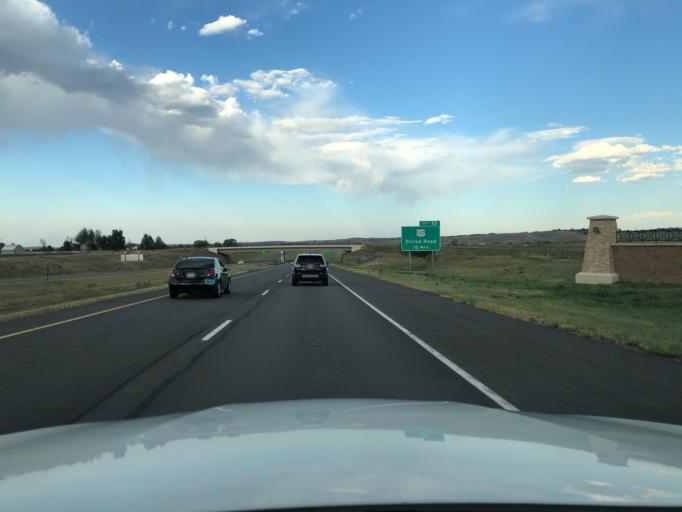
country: US
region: Colorado
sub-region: Boulder County
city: Louisville
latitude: 39.9554
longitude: -105.1128
